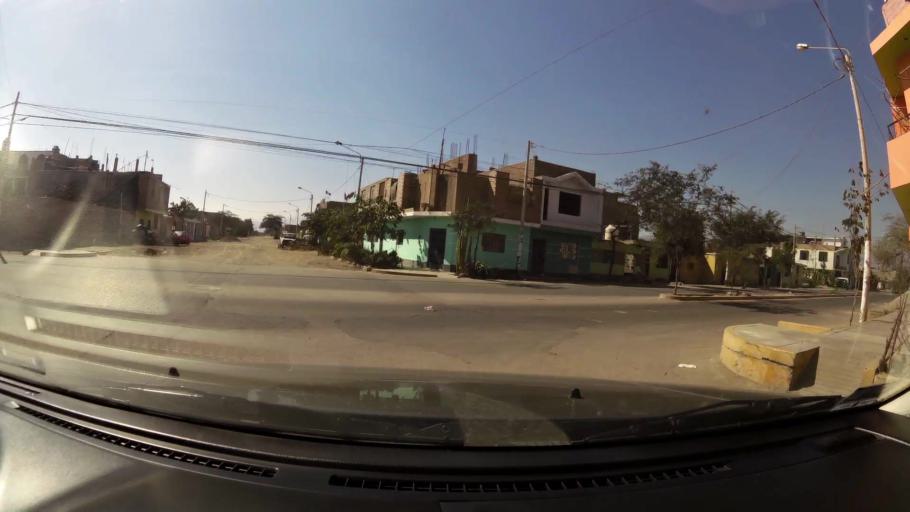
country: PE
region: Ica
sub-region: Provincia de Ica
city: La Tinguina
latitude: -14.0371
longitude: -75.7035
